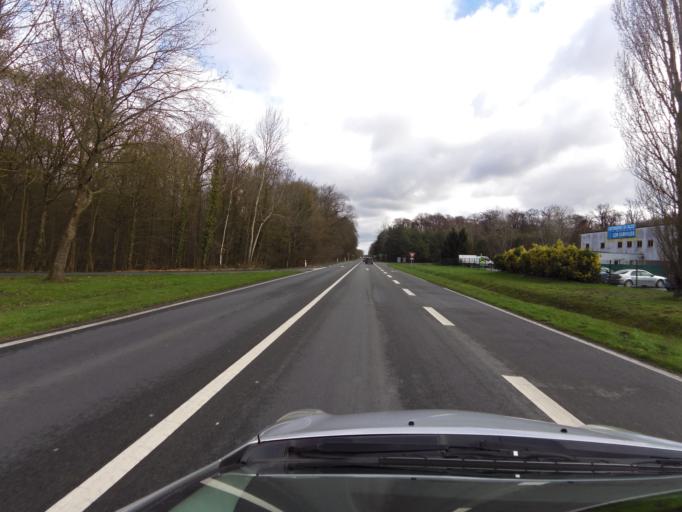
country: FR
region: Picardie
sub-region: Departement de l'Oise
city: Fleurines
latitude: 49.2737
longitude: 2.5919
